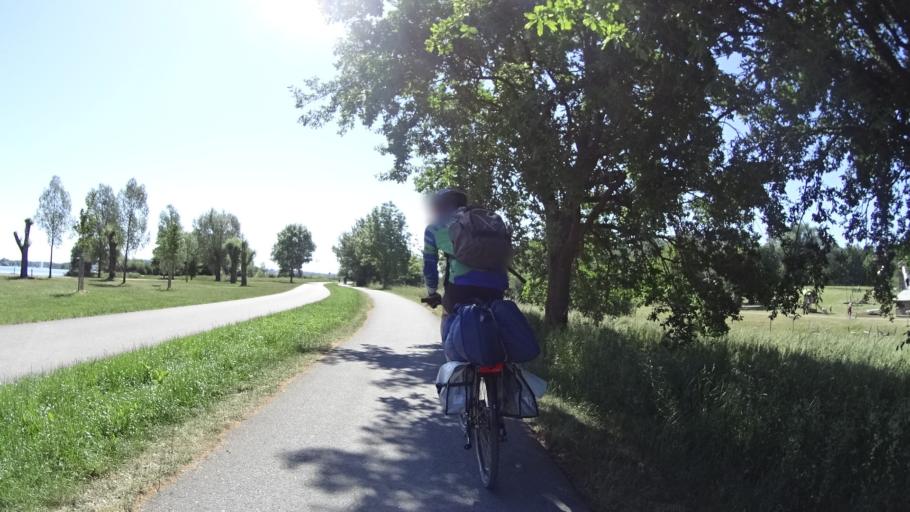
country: DE
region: Bavaria
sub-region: Regierungsbezirk Mittelfranken
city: Muhr am See
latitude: 49.1235
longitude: 10.7218
